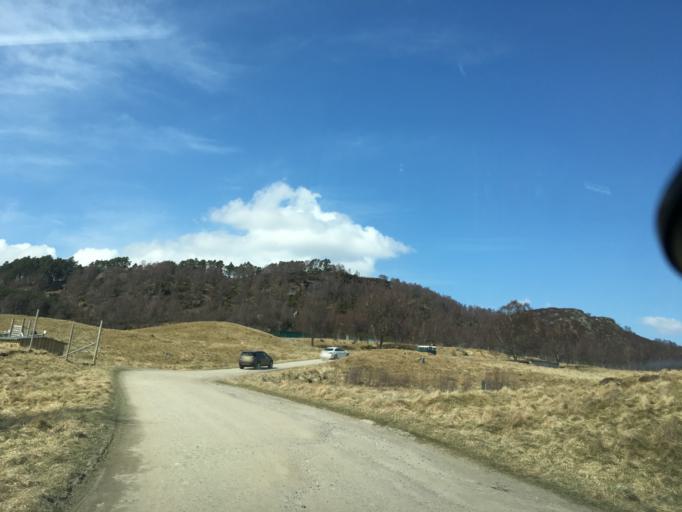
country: GB
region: Scotland
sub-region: Highland
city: Kingussie
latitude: 57.1091
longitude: -3.9811
